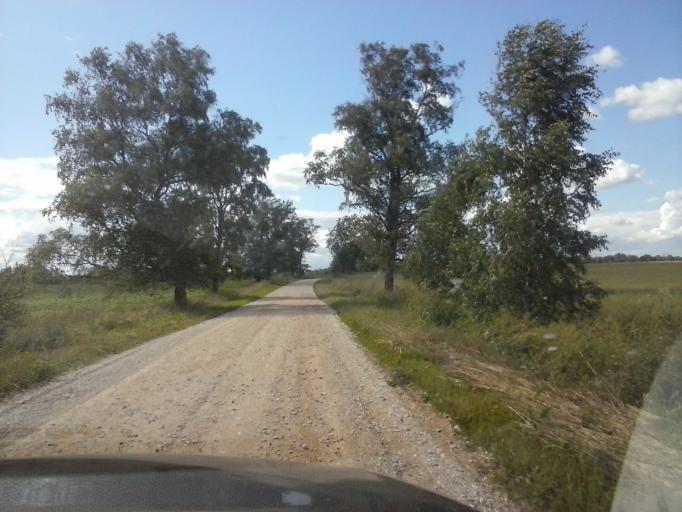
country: EE
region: Laeaene-Virumaa
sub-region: Vaeike-Maarja vald
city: Vaike-Maarja
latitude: 59.0818
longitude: 26.1931
